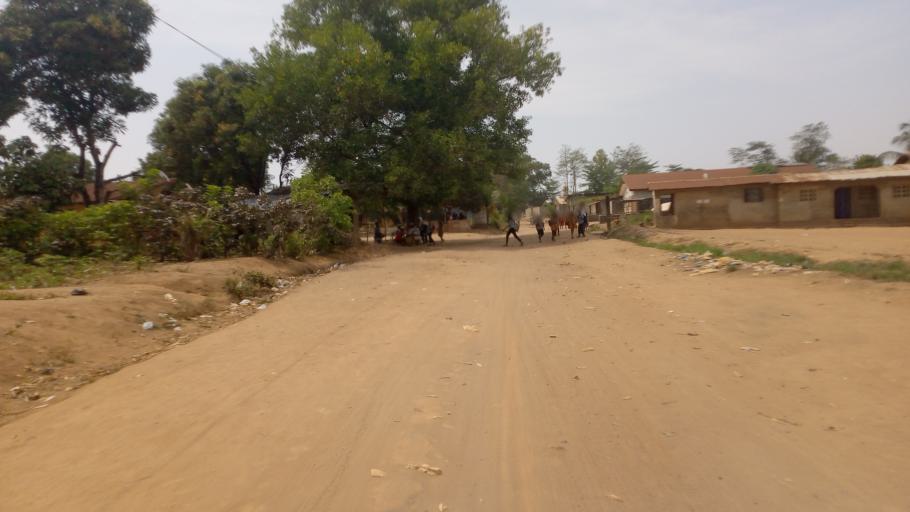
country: SL
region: Western Area
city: Waterloo
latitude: 8.3142
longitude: -13.0652
